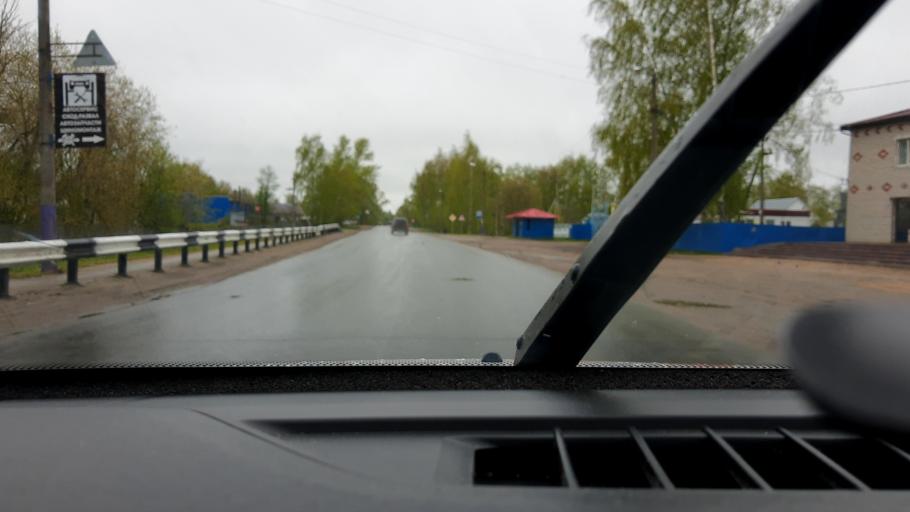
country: RU
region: Nizjnij Novgorod
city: Buturlino
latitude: 55.5738
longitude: 44.8801
